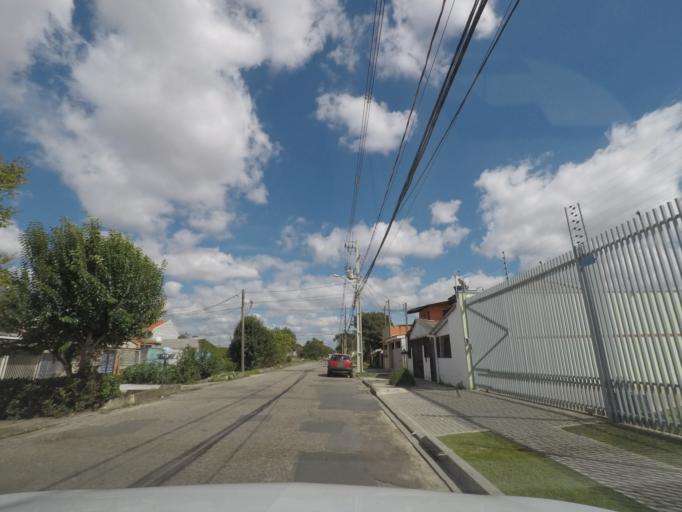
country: BR
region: Parana
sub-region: Sao Jose Dos Pinhais
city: Sao Jose dos Pinhais
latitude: -25.4990
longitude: -49.2267
